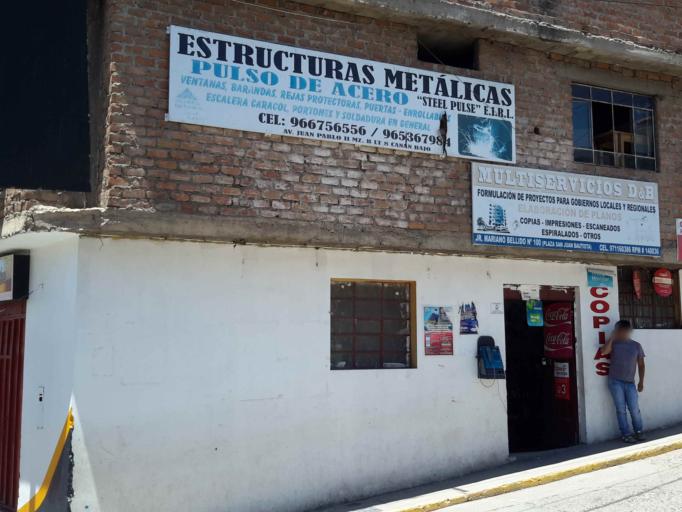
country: PE
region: Ayacucho
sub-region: Provincia de Huamanga
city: Ayacucho
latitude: -13.1665
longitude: -74.2236
